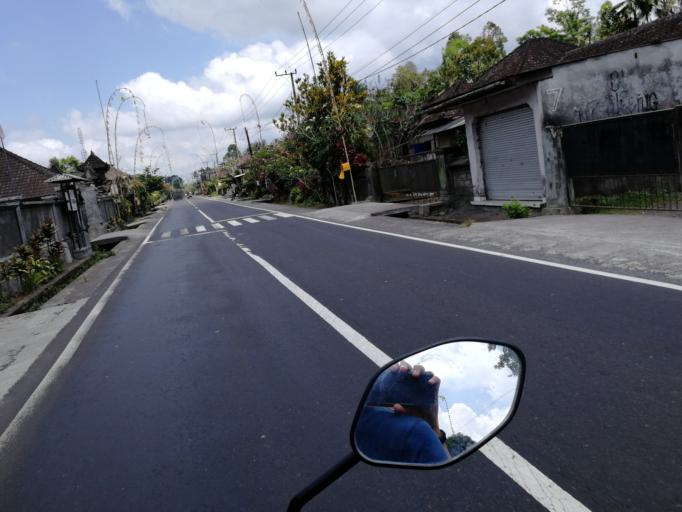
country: ID
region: Bali
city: Banjar Kubu
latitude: -8.4286
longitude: 115.4276
